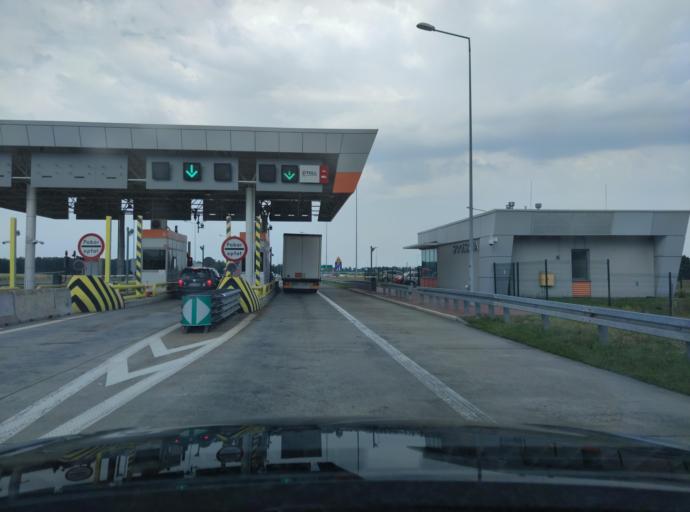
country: PL
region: Opole Voivodeship
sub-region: Powiat strzelecki
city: Strzelce Opolskie
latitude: 50.4620
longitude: 18.2726
